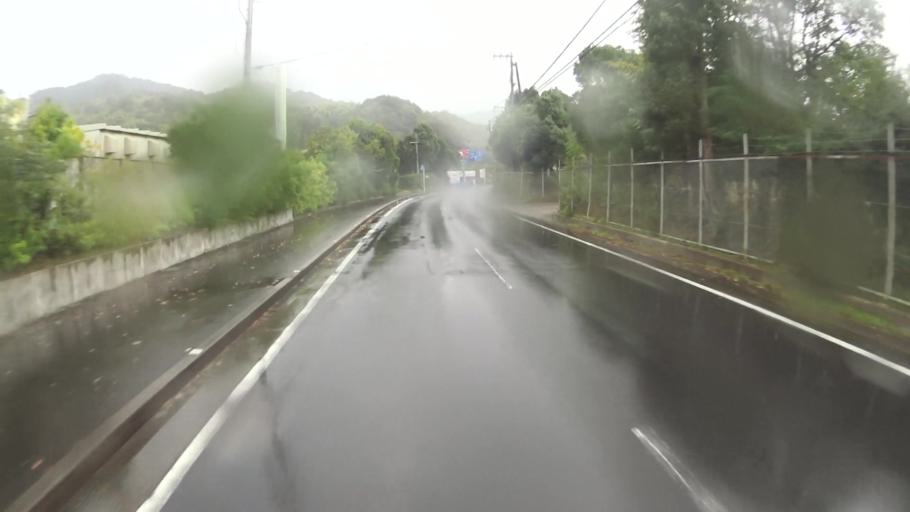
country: JP
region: Kyoto
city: Miyazu
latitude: 35.5504
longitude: 135.2112
